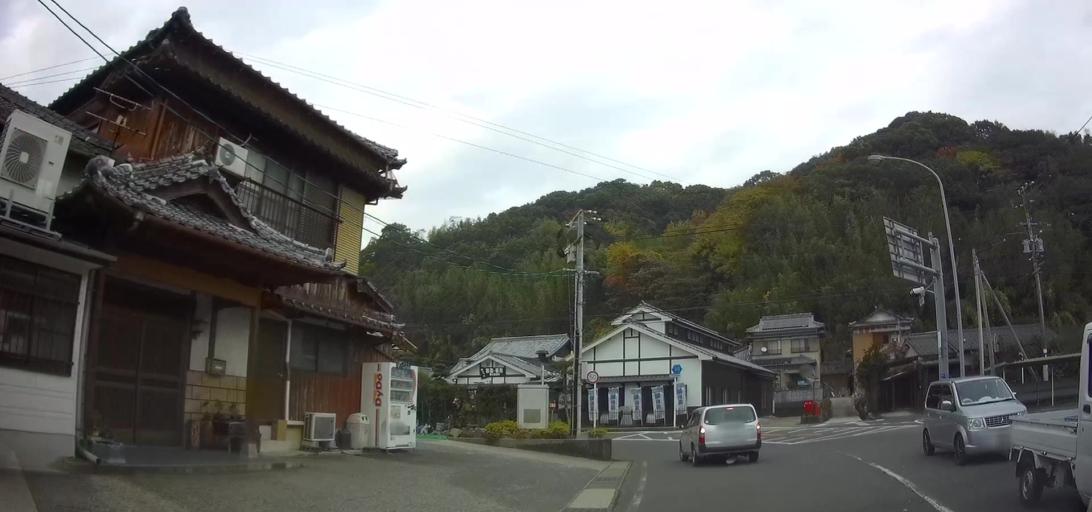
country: JP
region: Nagasaki
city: Shimabara
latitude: 32.6540
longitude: 130.2620
